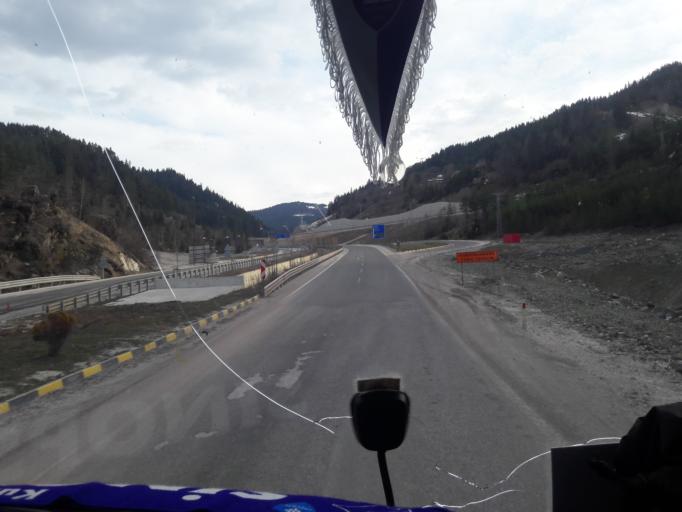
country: TR
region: Kastamonu
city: Kuzyaka
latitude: 41.1053
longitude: 33.7505
